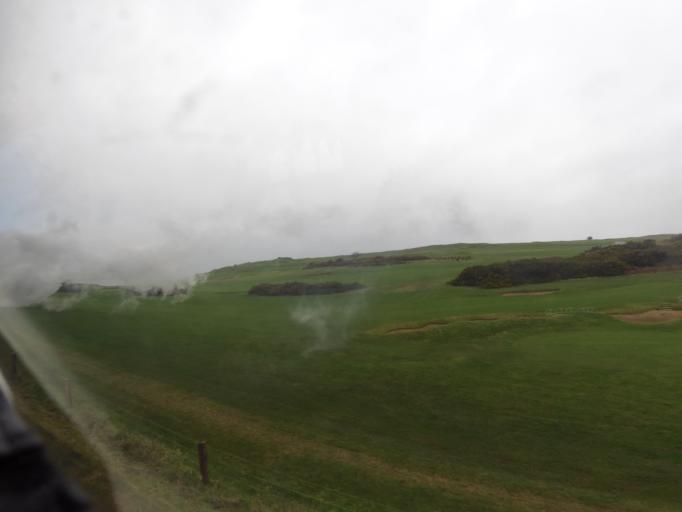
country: GB
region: England
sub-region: Norfolk
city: Sheringham
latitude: 52.9433
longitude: 1.1931
